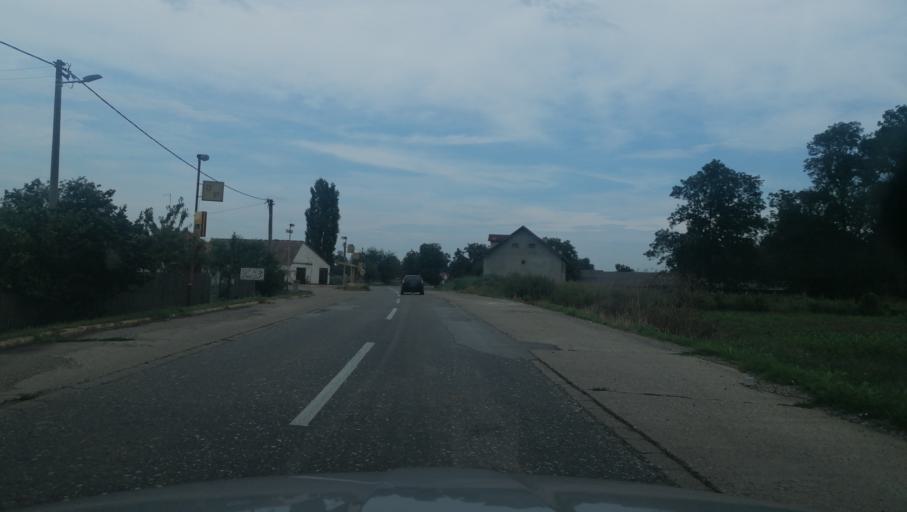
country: RS
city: Klenje
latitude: 44.8153
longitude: 19.4437
